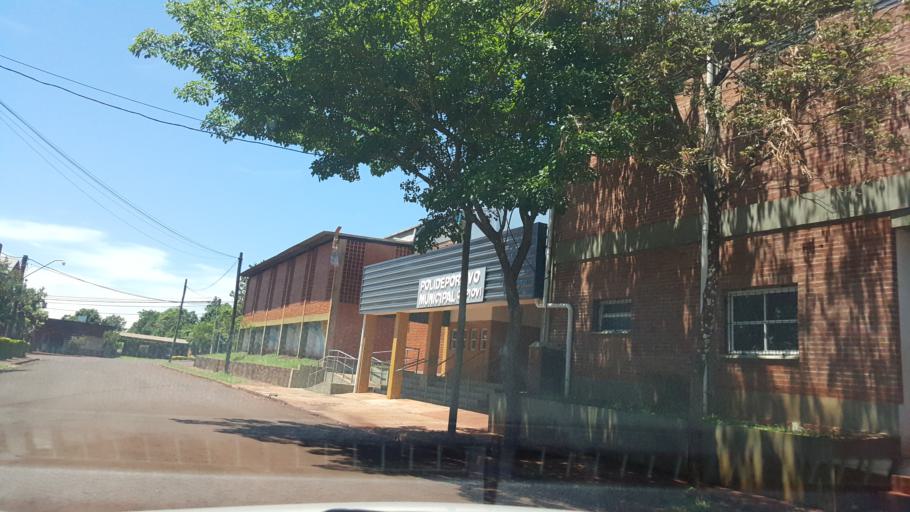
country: AR
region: Misiones
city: Capiovi
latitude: -26.9331
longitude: -55.0587
